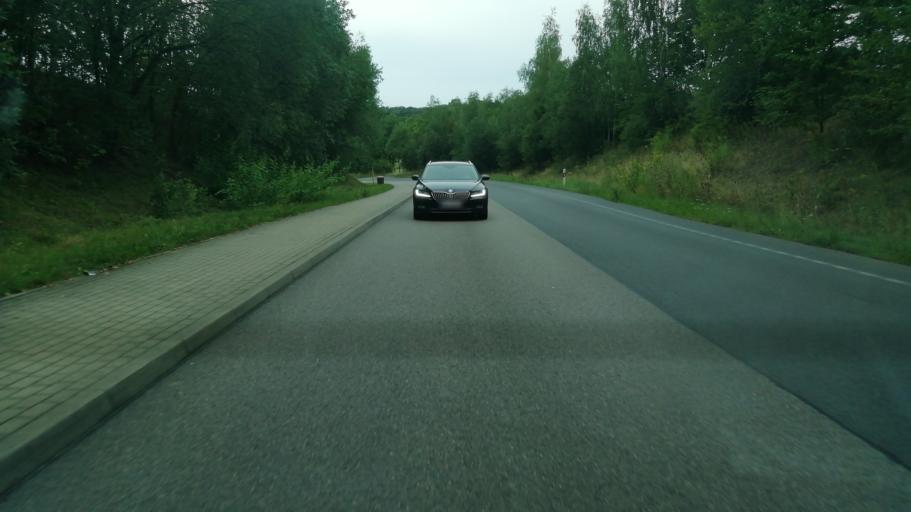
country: DE
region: Saxony
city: Wilsdruff
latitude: 51.0589
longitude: 13.5355
